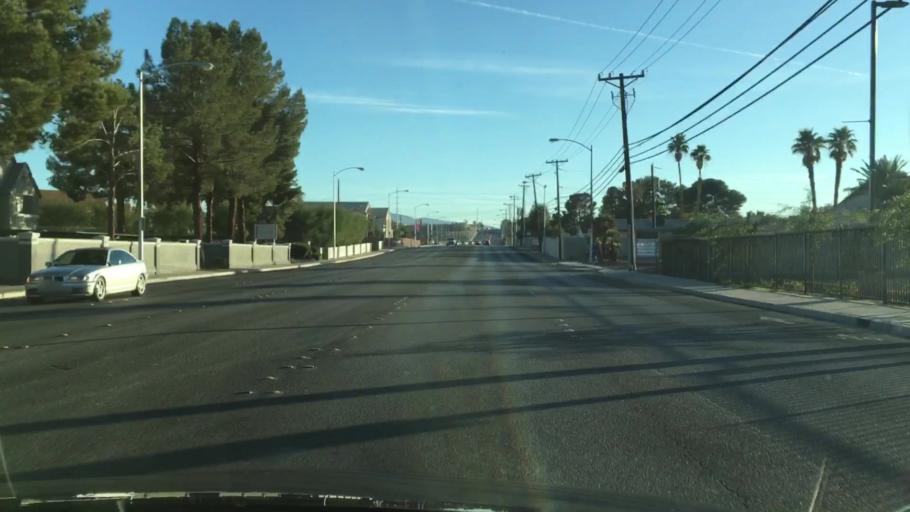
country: US
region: Nevada
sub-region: Clark County
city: Whitney
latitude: 36.0891
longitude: -115.0732
